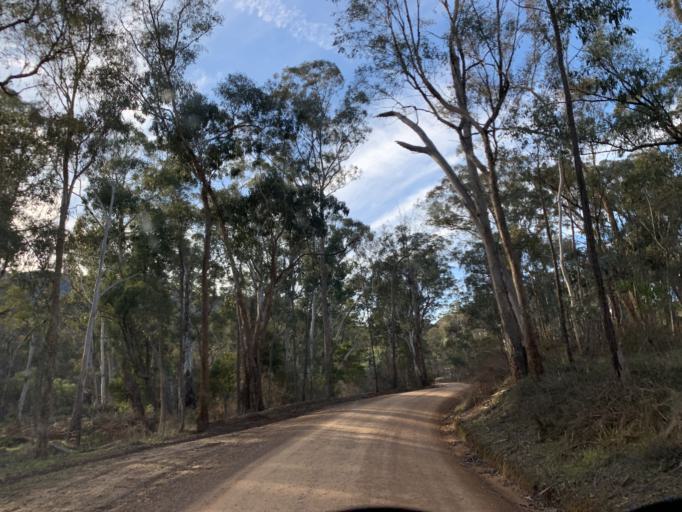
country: AU
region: Victoria
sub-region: Mansfield
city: Mansfield
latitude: -36.9373
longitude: 146.0953
